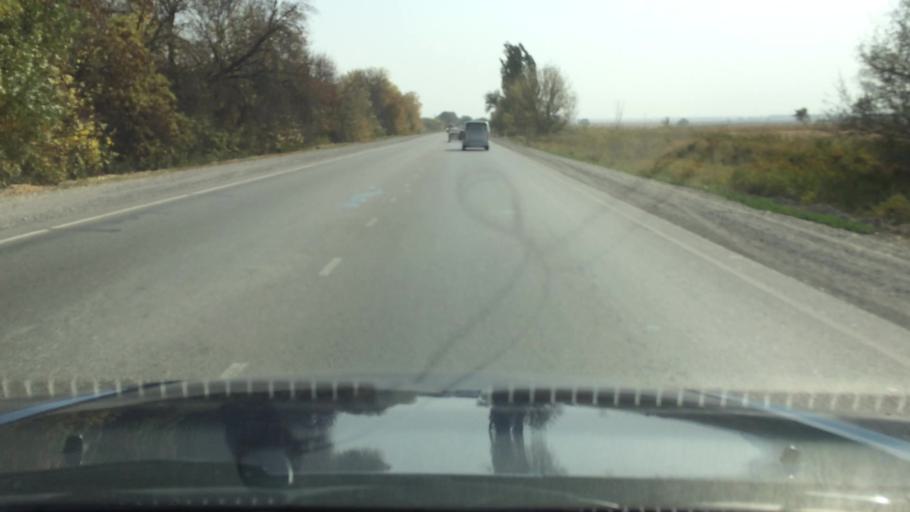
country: KG
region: Chuy
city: Lebedinovka
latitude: 42.9273
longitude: 74.6971
